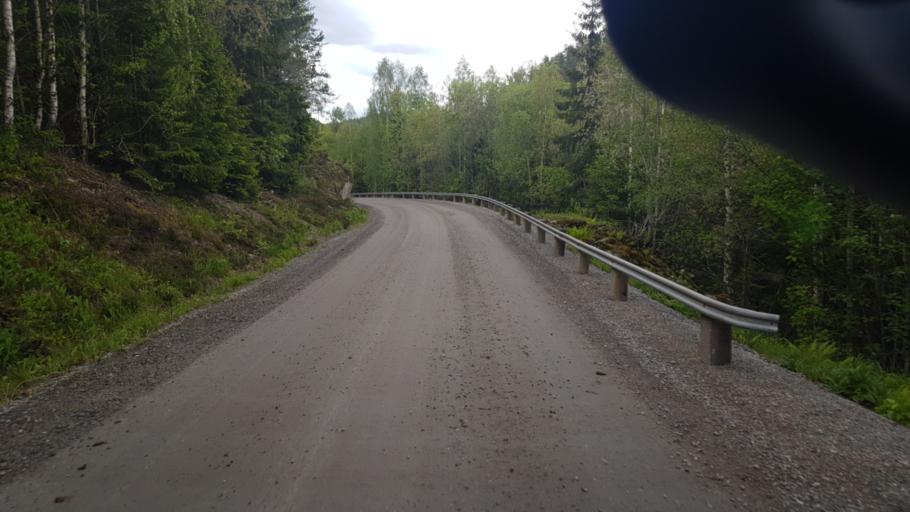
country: NO
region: Ostfold
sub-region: Romskog
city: Romskog
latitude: 59.7131
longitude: 11.9838
